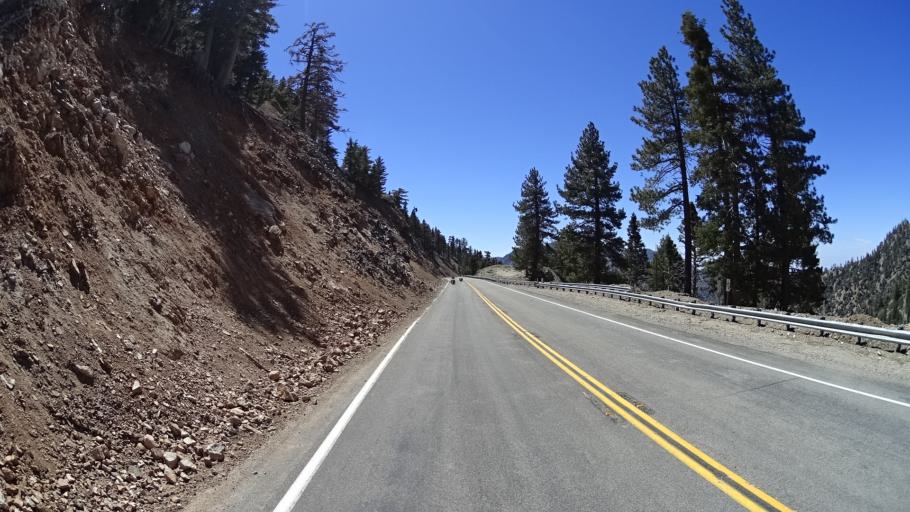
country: US
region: California
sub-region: San Bernardino County
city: Wrightwood
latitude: 34.3481
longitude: -117.8111
